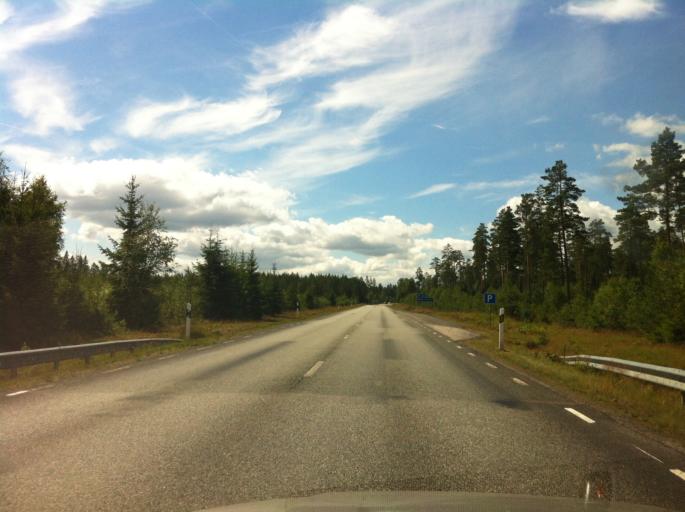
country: SE
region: Joenkoeping
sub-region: Gislaveds Kommun
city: Gislaved
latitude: 57.3734
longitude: 13.5770
